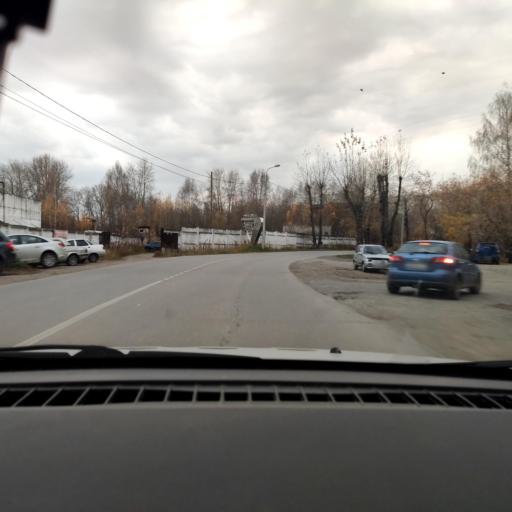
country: RU
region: Perm
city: Polazna
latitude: 58.1202
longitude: 56.3871
